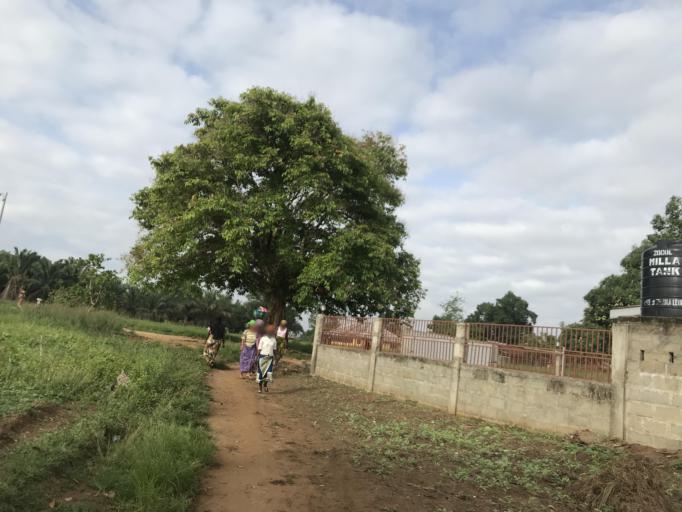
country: SL
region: Eastern Province
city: Pendembu
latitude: 8.1006
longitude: -10.6920
